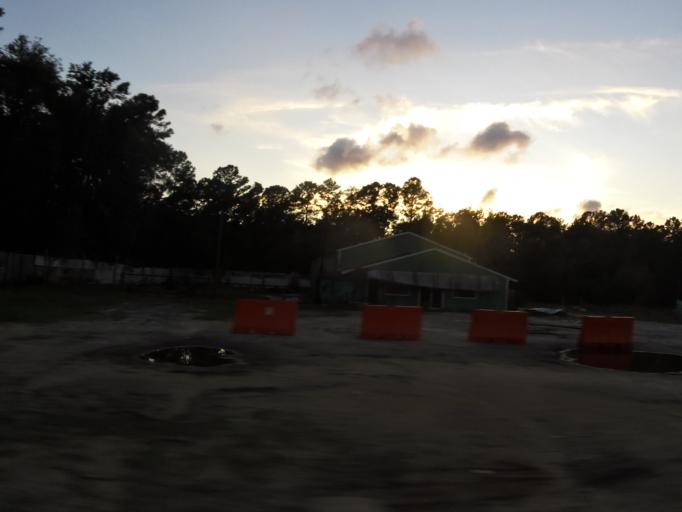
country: US
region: Georgia
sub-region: Camden County
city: Kingsland
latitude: 30.7895
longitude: -81.6881
